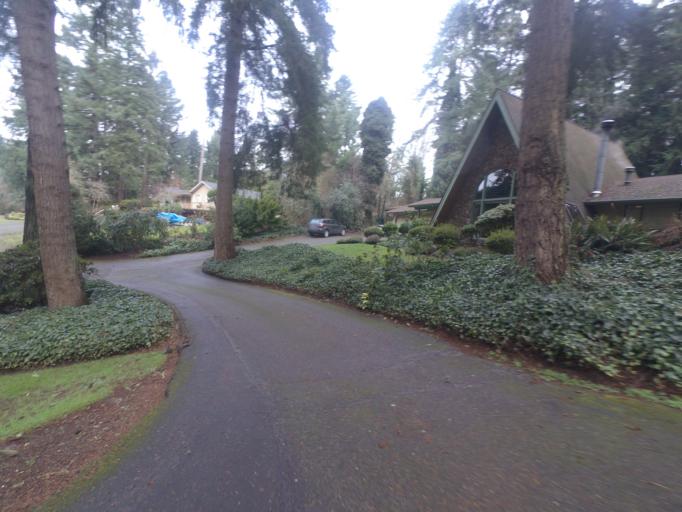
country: US
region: Washington
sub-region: Pierce County
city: University Place
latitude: 47.2231
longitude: -122.5469
